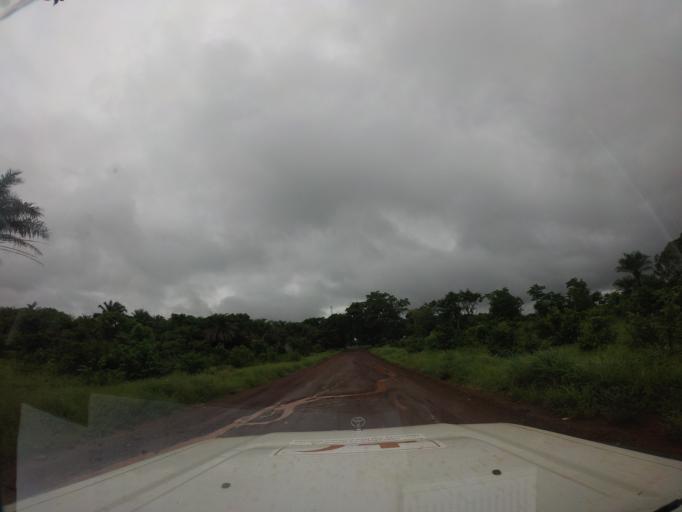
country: SL
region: Northern Province
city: Kambia
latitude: 9.1291
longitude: -12.8996
